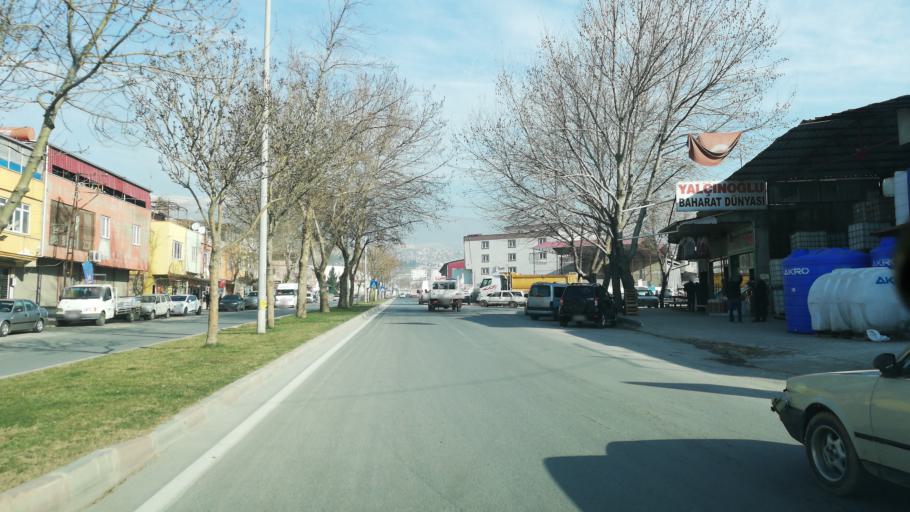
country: TR
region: Kahramanmaras
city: Kahramanmaras
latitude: 37.5629
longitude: 36.9174
